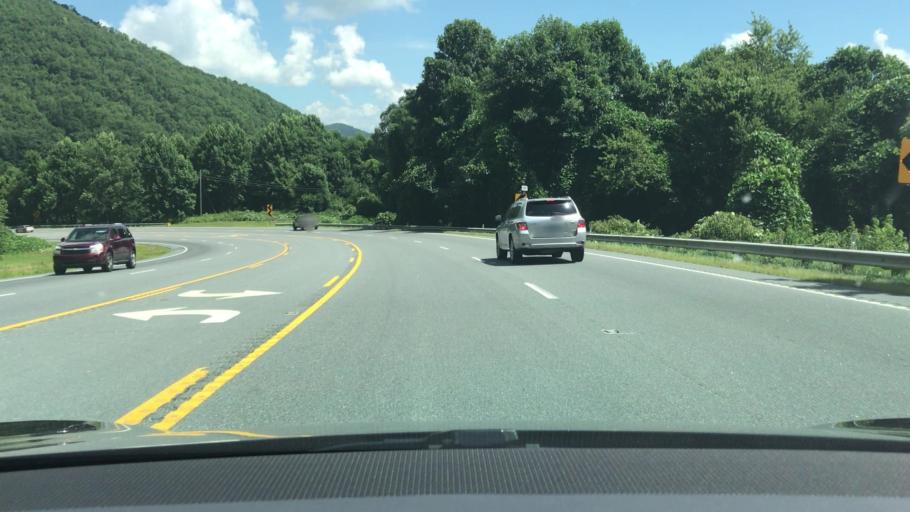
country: US
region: North Carolina
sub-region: Macon County
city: Franklin
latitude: 35.2620
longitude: -83.2986
